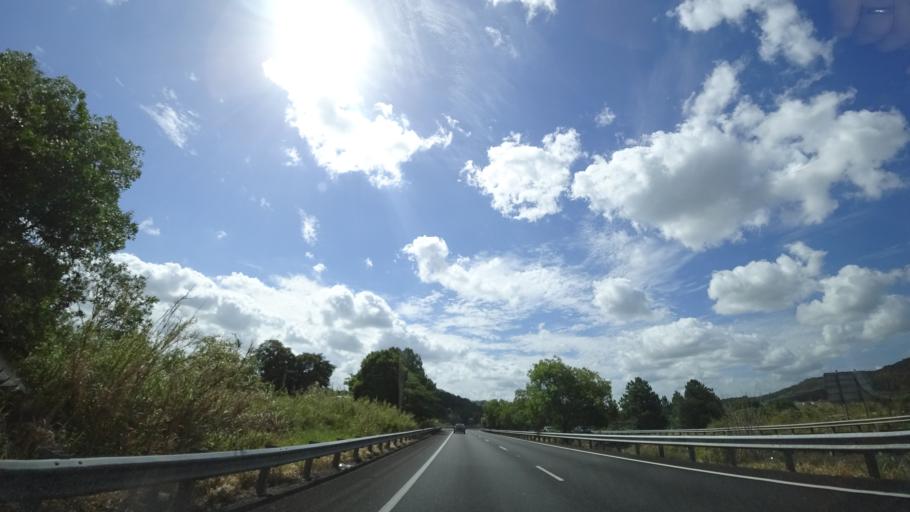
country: AU
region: Queensland
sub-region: Sunshine Coast
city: Twin Waters
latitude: -26.6205
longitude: 152.9847
